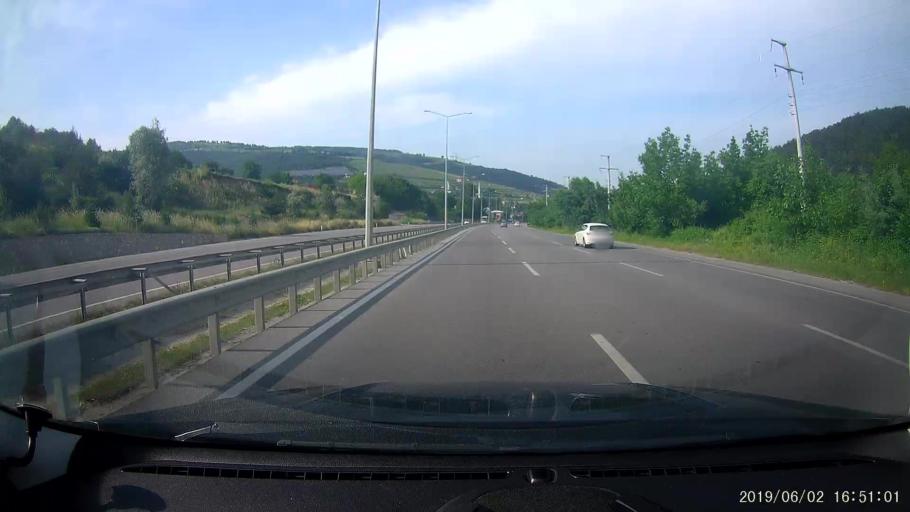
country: TR
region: Samsun
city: Taflan
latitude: 41.2668
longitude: 36.1773
